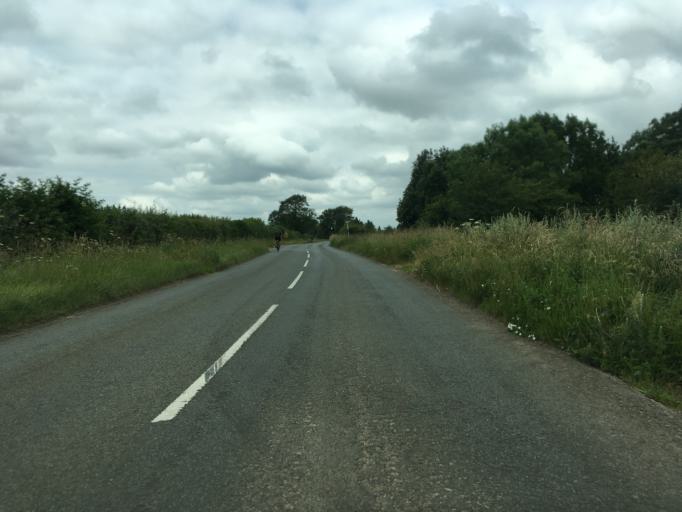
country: GB
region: England
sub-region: Oxfordshire
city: Chipping Norton
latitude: 51.9192
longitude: -1.5033
